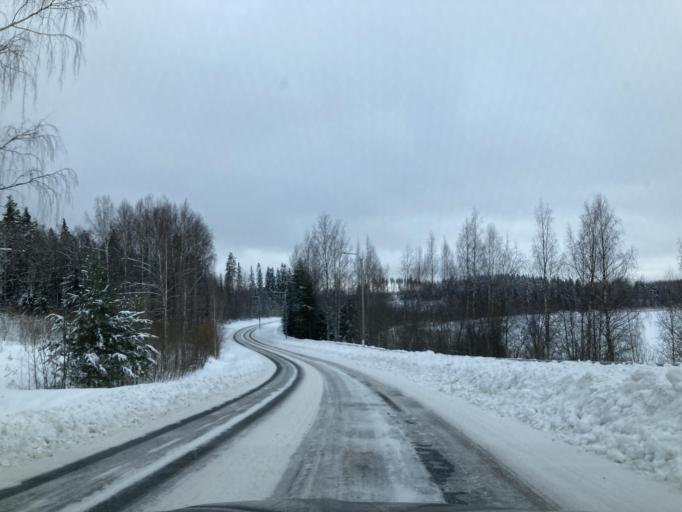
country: FI
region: Central Finland
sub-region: Jaemsae
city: Jaemsae
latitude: 61.8742
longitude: 25.2703
